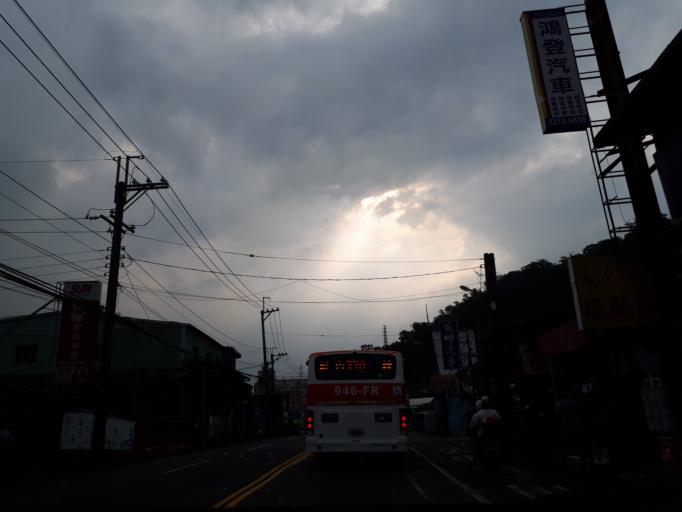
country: TW
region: Taipei
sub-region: Taipei
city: Banqiao
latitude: 24.9573
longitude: 121.5015
